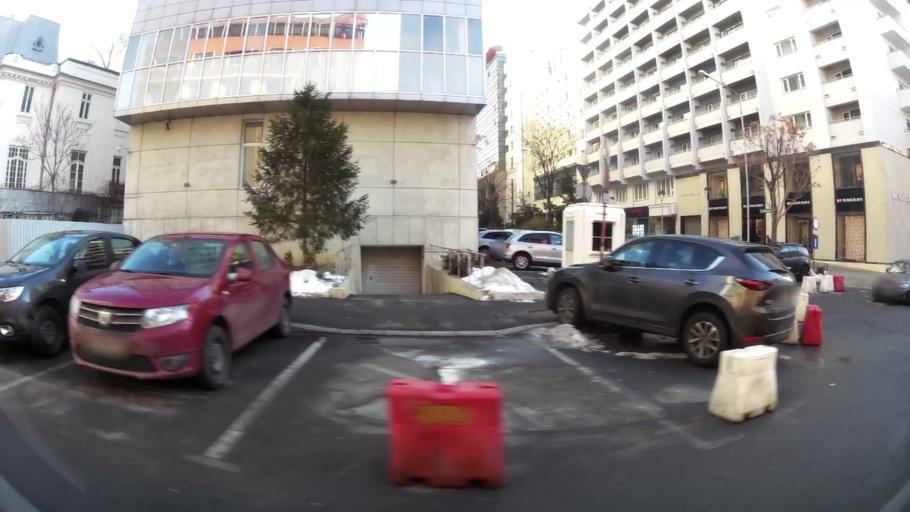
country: RO
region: Bucuresti
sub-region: Municipiul Bucuresti
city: Bucuresti
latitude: 44.4416
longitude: 26.0925
